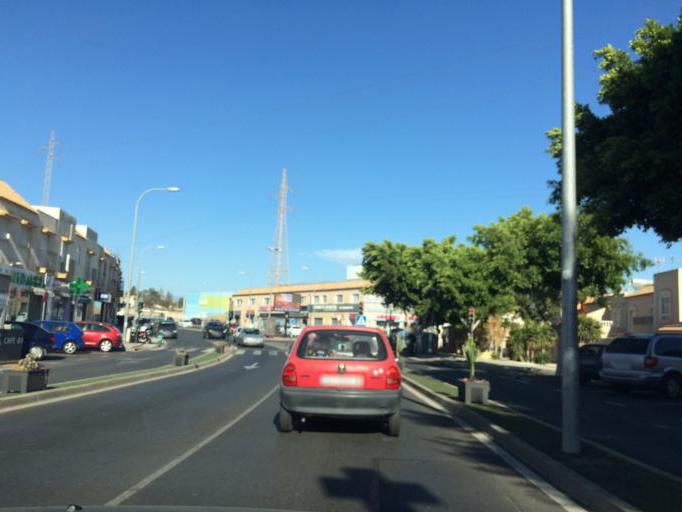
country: ES
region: Andalusia
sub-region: Provincia de Almeria
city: Huercal de Almeria
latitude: 36.8694
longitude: -2.4395
